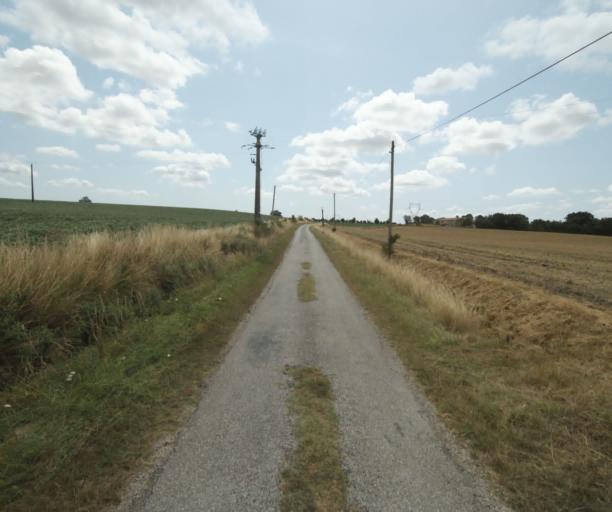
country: FR
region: Midi-Pyrenees
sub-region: Departement de la Haute-Garonne
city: Saint-Felix-Lauragais
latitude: 43.4192
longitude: 1.9044
